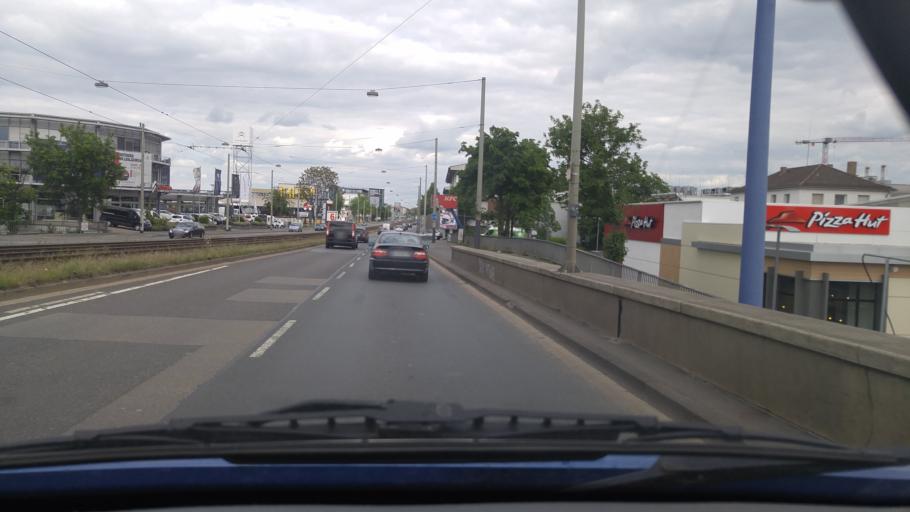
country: DE
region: Hesse
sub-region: Regierungsbezirk Darmstadt
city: Offenbach
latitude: 50.1192
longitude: 8.7329
